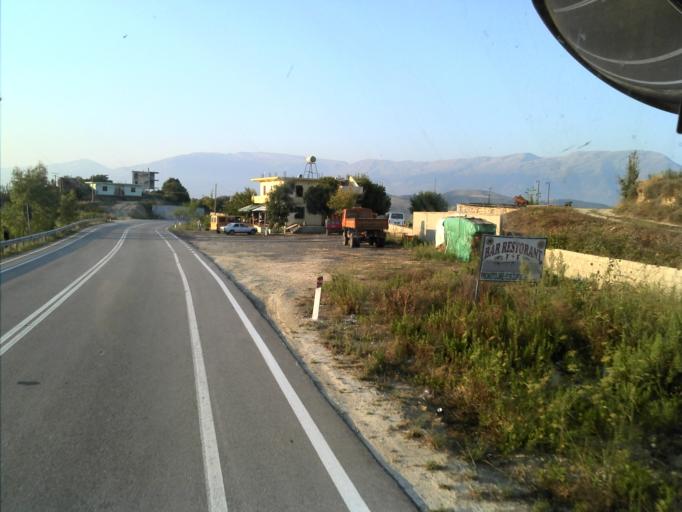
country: AL
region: Fier
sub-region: Rrethi i Mallakastres
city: Fratar
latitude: 40.4899
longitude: 19.8401
